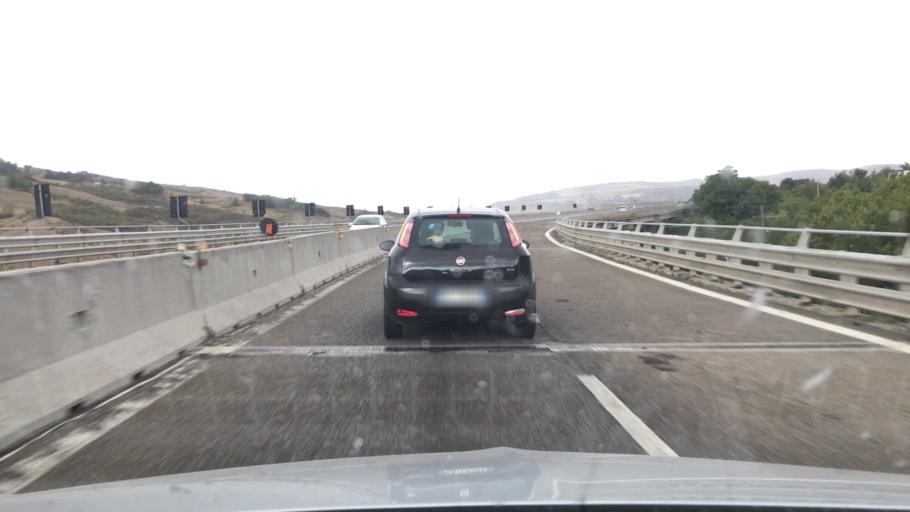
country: IT
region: Basilicate
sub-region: Provincia di Potenza
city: Vaglio Basilicata
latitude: 40.6496
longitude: 15.9009
